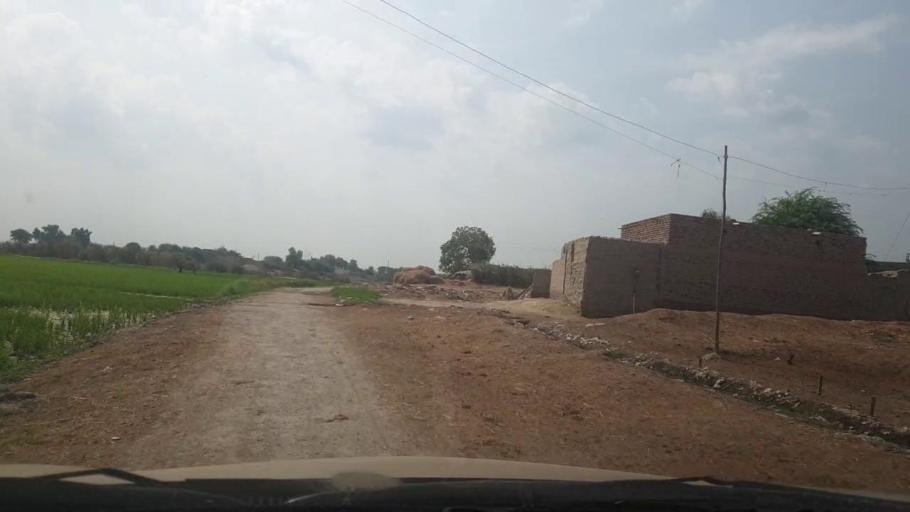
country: PK
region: Sindh
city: Larkana
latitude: 27.6490
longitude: 68.2106
